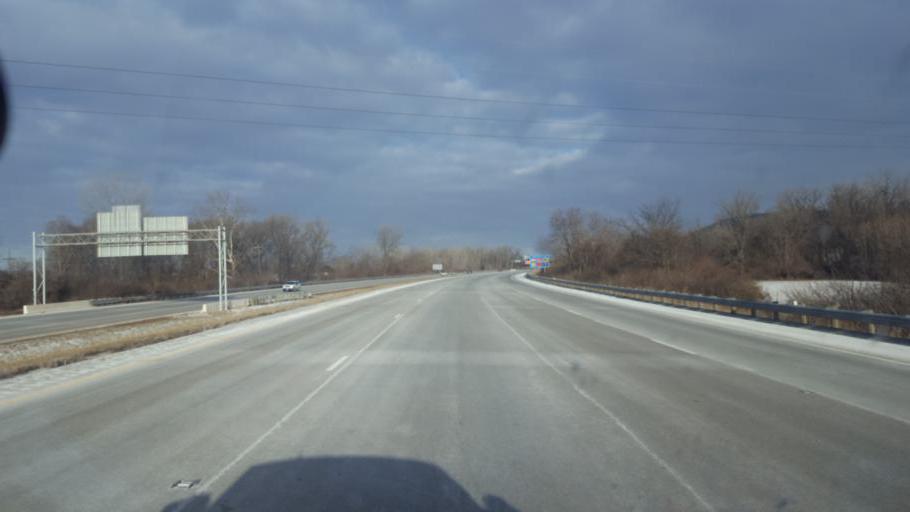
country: US
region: Ohio
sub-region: Ross County
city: Chillicothe
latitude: 39.3260
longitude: -82.9440
